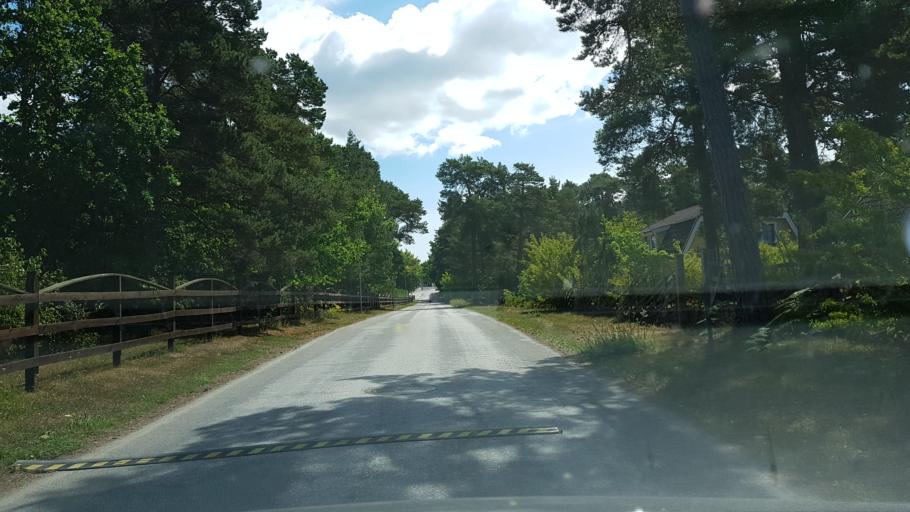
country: SE
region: Gotland
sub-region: Gotland
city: Visby
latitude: 57.8008
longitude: 18.5099
